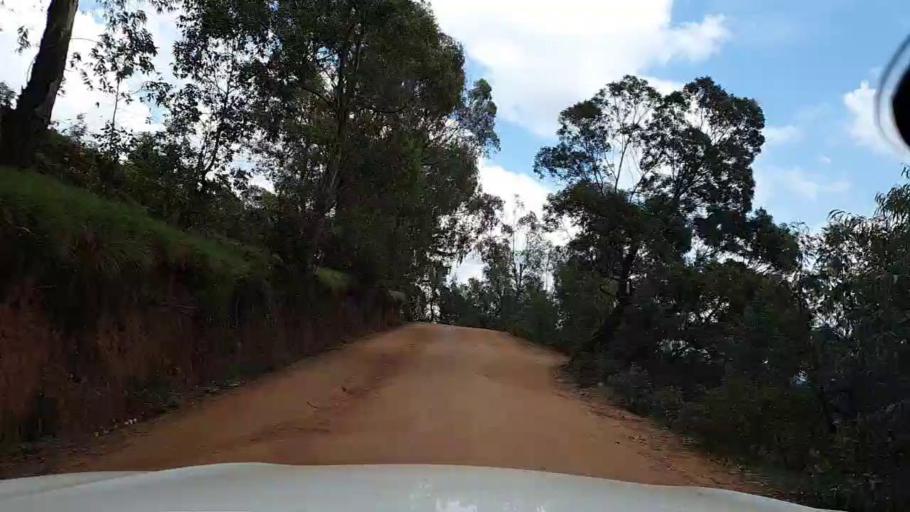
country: RW
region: Southern Province
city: Nzega
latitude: -2.7086
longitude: 29.5226
